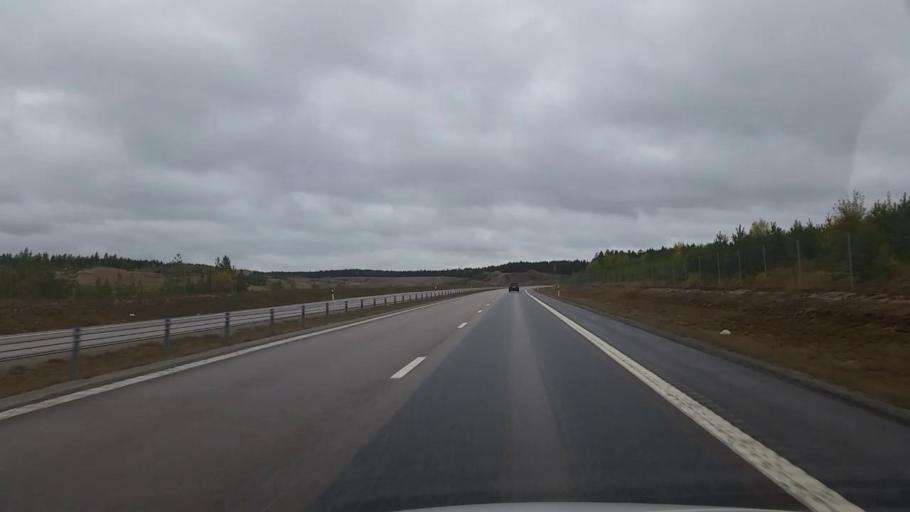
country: SE
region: Uppsala
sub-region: Osthammars Kommun
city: Bjorklinge
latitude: 60.1132
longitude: 17.5530
